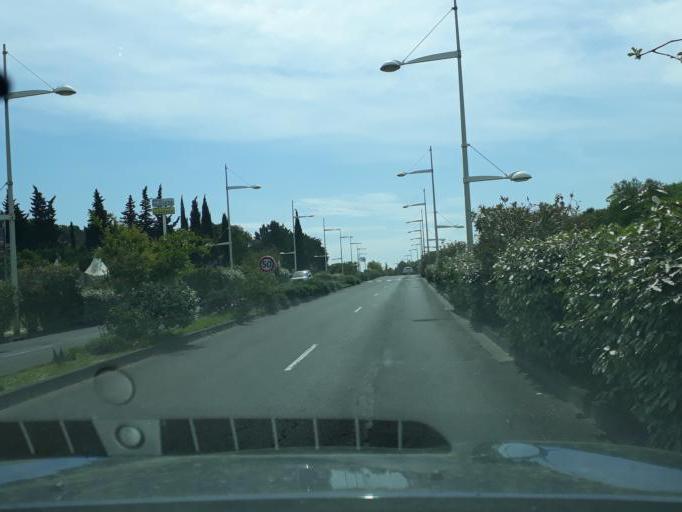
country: FR
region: Languedoc-Roussillon
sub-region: Departement de l'Herault
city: Agde
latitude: 43.2979
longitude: 3.4944
